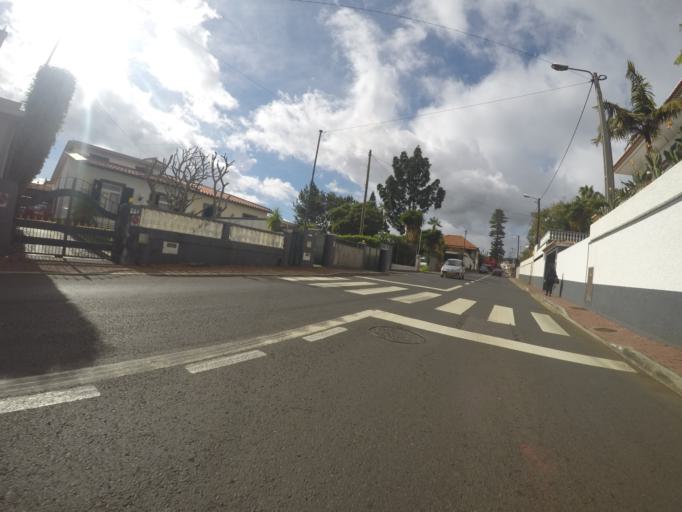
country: PT
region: Madeira
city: Camara de Lobos
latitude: 32.6558
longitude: -16.9410
